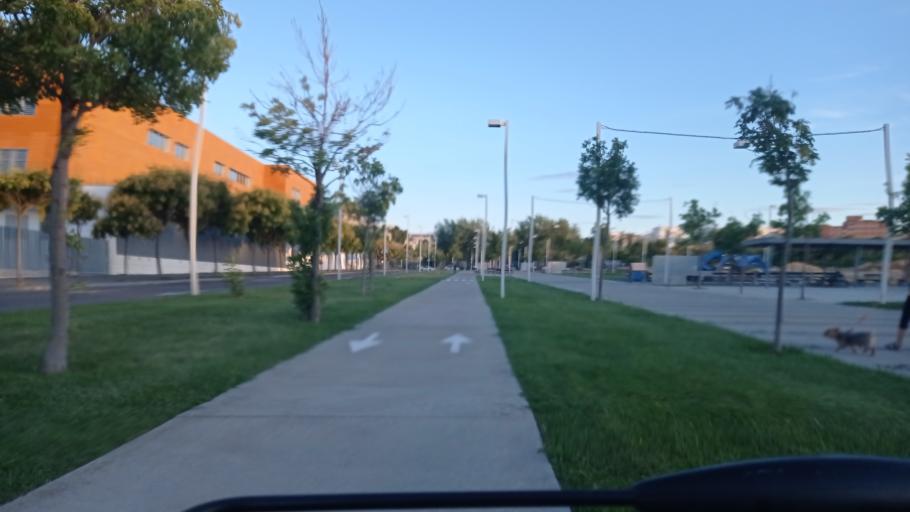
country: ES
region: Aragon
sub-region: Provincia de Zaragoza
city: Oliver-Valdefierro, Oliver, Valdefierro
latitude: 41.6580
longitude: -0.9248
